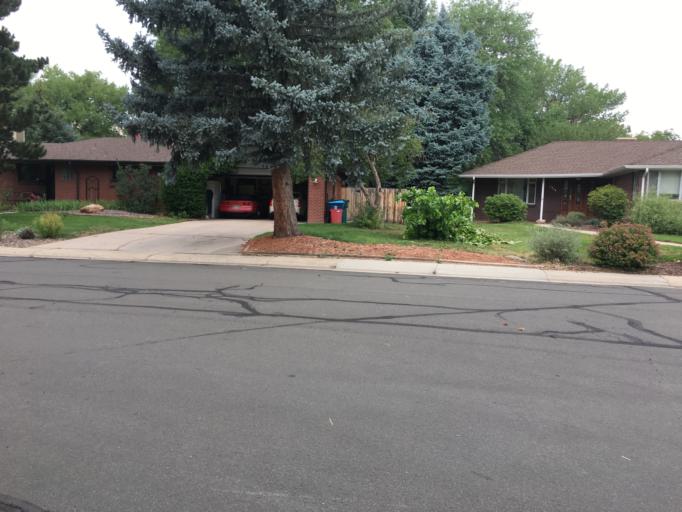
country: US
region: Colorado
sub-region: Arapahoe County
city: Glendale
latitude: 39.6724
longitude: -104.9268
